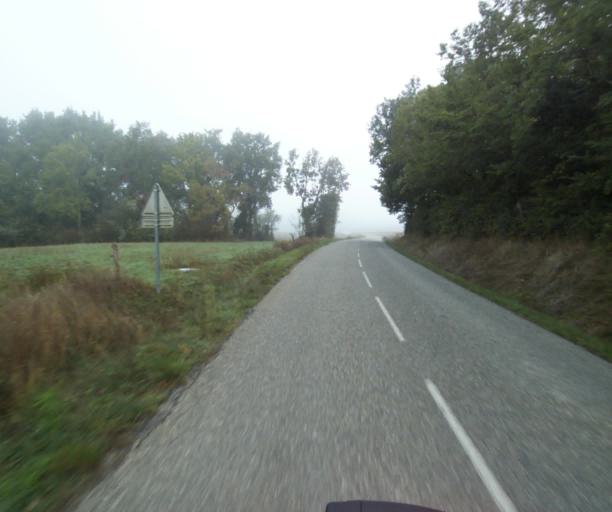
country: FR
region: Midi-Pyrenees
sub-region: Departement du Tarn-et-Garonne
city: Orgueil
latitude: 43.9342
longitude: 1.4191
